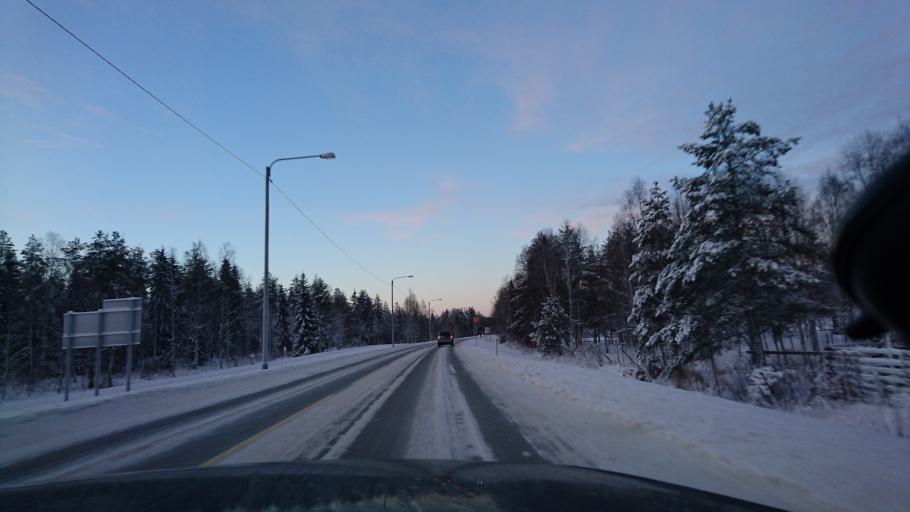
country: FI
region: Lapland
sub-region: Rovaniemi
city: Ranua
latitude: 65.9332
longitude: 26.5002
